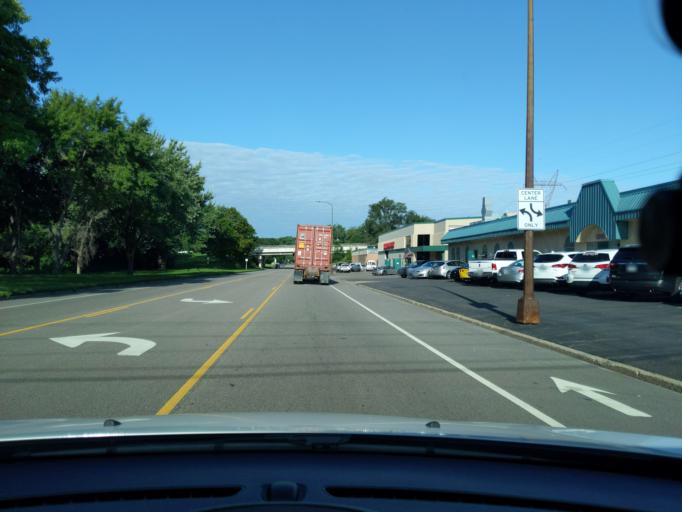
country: US
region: Minnesota
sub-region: Ramsey County
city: Falcon Heights
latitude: 44.9665
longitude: -93.1442
